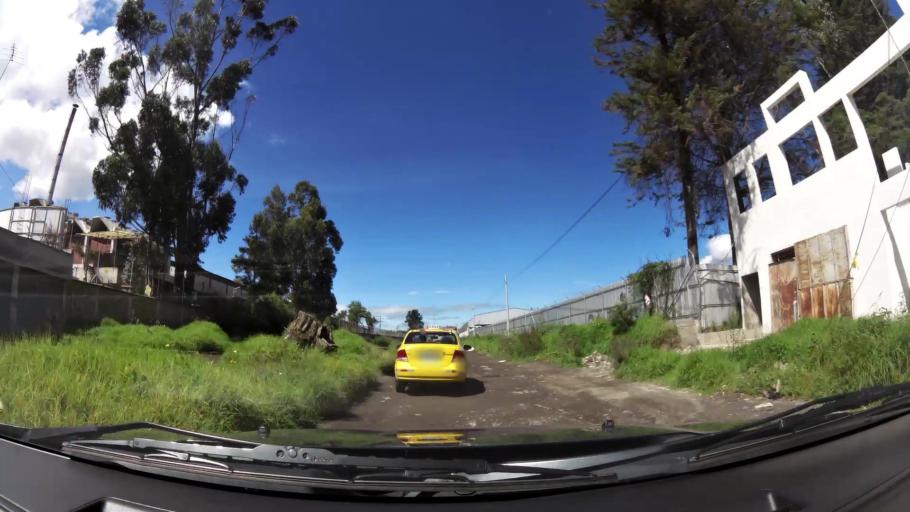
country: EC
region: Pichincha
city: Quito
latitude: -0.3009
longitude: -78.5476
